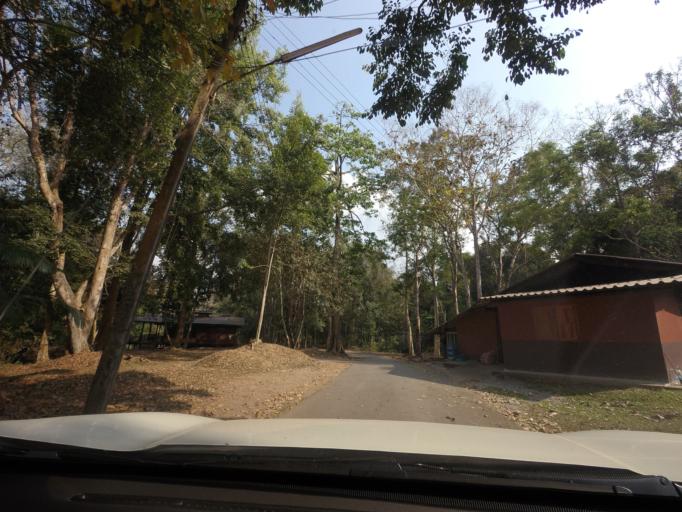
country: TH
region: Nakhon Ratchasima
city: Pak Chong
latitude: 14.4380
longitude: 101.3737
